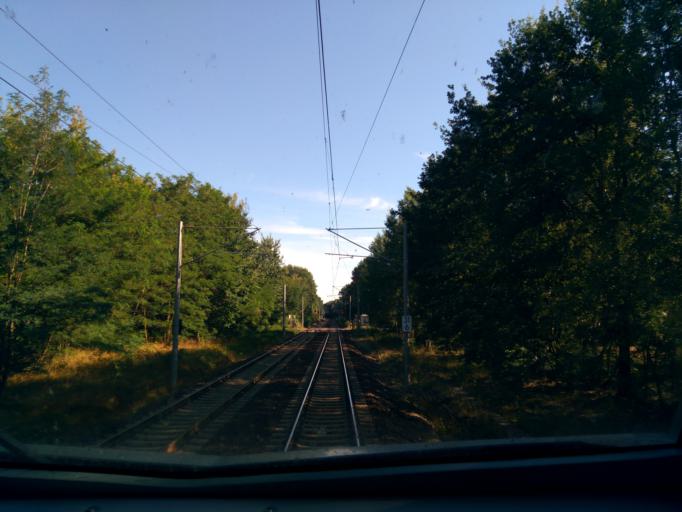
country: DE
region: Brandenburg
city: Bestensee
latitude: 52.2612
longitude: 13.6345
